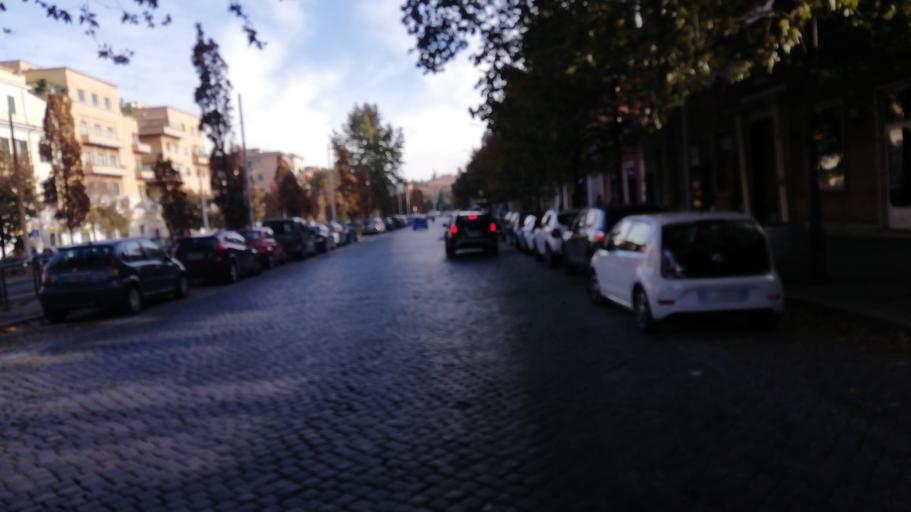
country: IT
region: Latium
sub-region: Citta metropolitana di Roma Capitale
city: Rome
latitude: 41.8810
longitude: 12.4850
